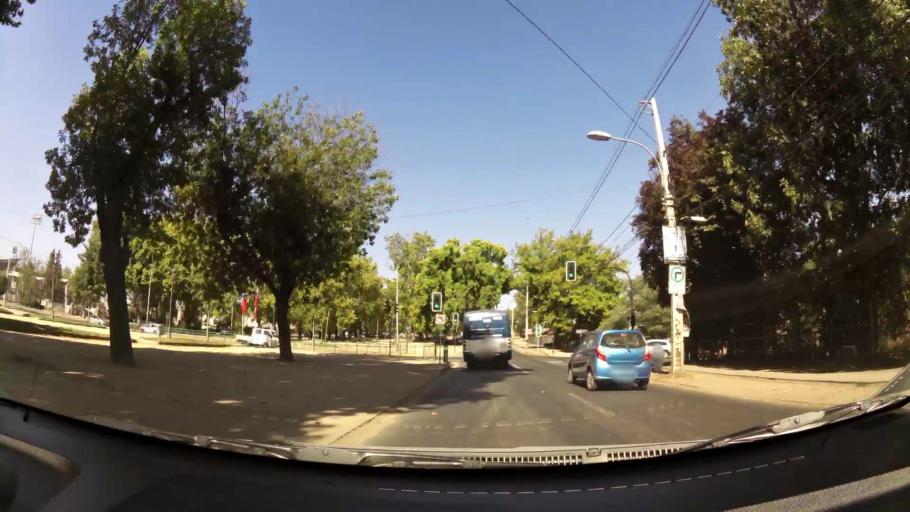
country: CL
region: Maule
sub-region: Provincia de Talca
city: Talca
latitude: -35.4214
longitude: -71.6759
